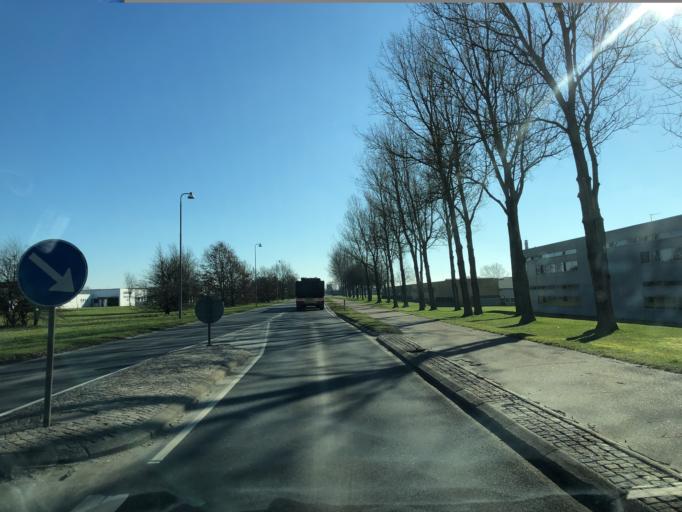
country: DK
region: Central Jutland
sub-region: Ikast-Brande Kommune
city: Ikast
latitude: 56.1310
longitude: 9.1667
